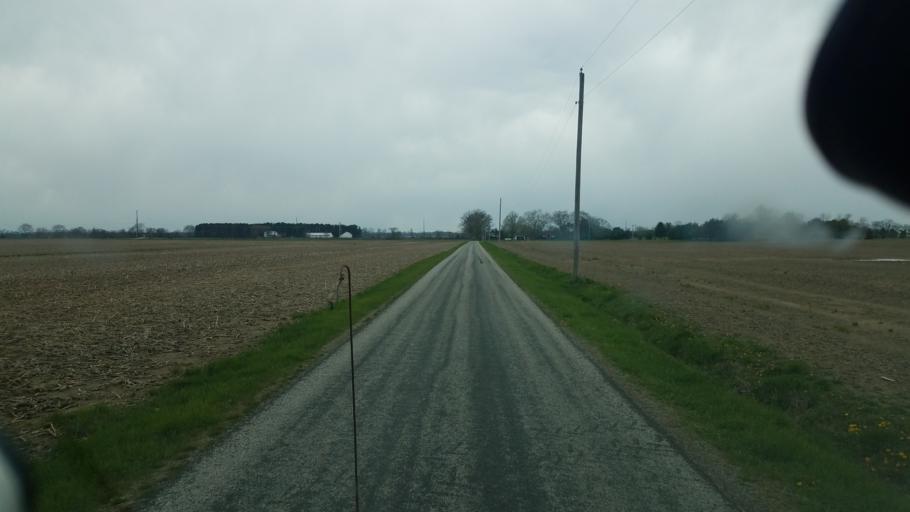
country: US
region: Ohio
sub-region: Marion County
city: Prospect
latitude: 40.4050
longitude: -83.1387
